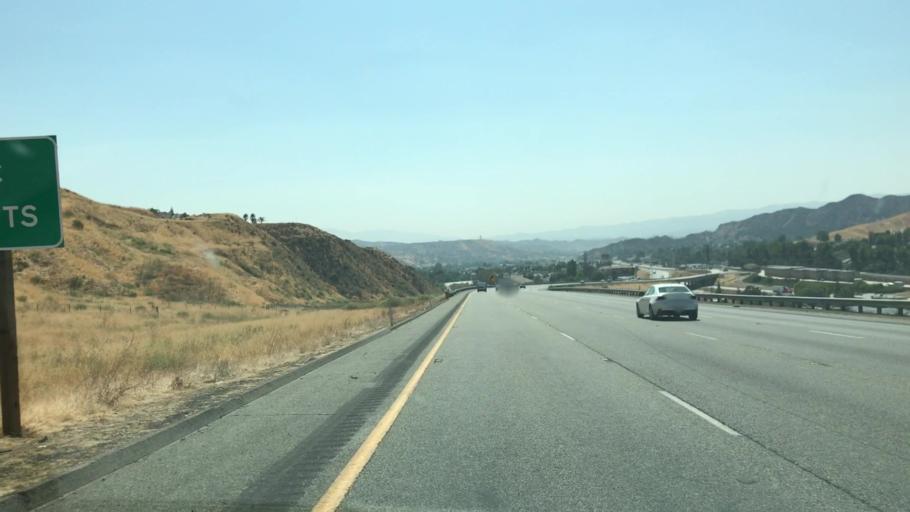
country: US
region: California
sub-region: Los Angeles County
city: Castaic
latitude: 34.5086
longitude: -118.6300
